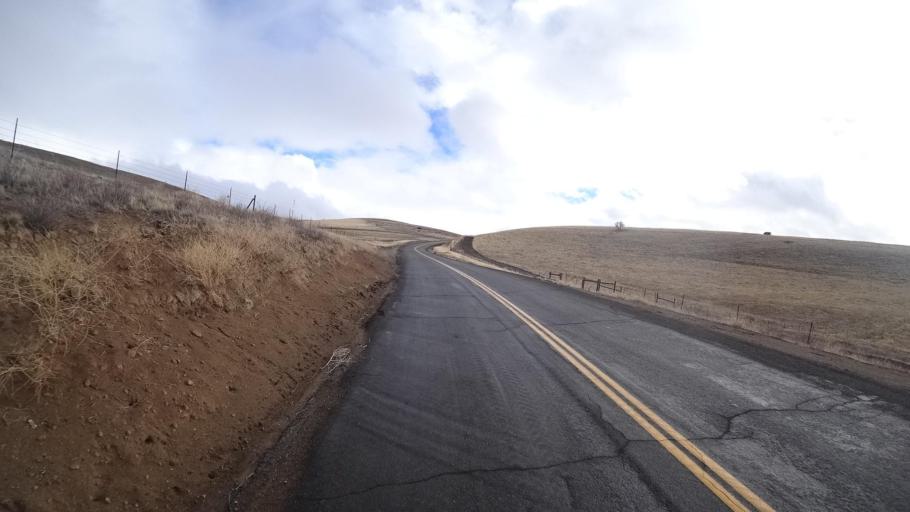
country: US
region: California
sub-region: Kern County
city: Maricopa
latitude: 34.9163
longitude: -119.4066
